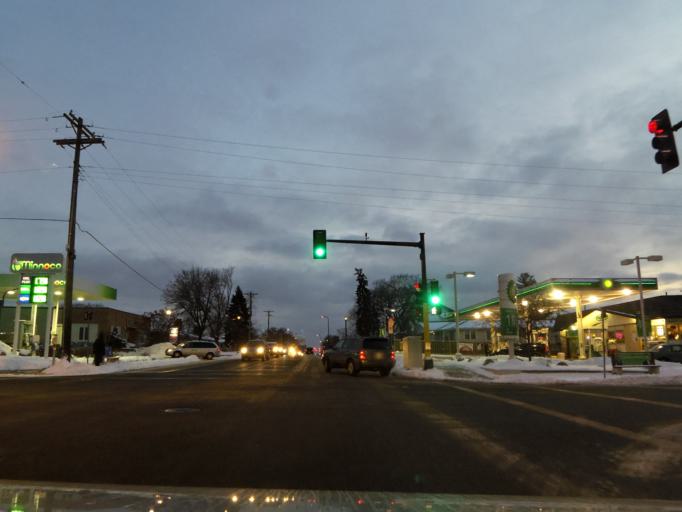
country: US
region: Minnesota
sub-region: Hennepin County
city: Richfield
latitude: 44.8944
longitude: -93.3087
